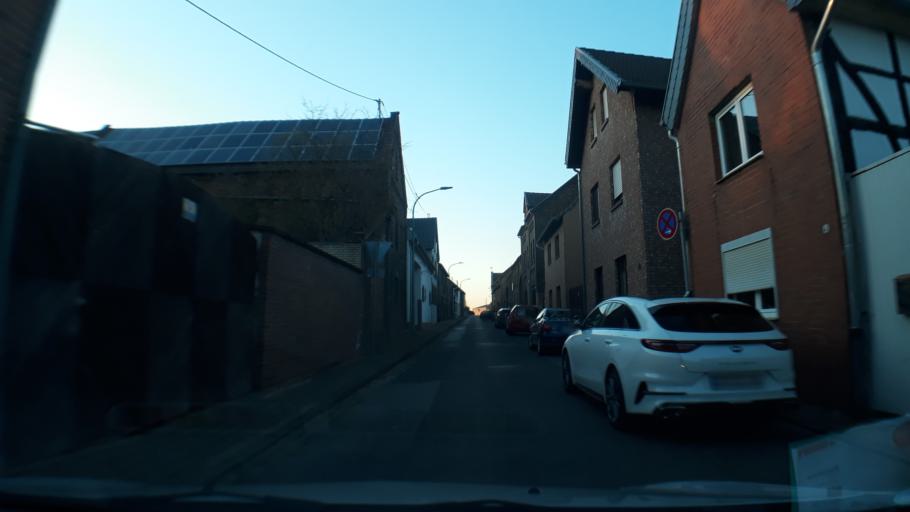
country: DE
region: North Rhine-Westphalia
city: Zulpich
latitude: 50.7028
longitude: 6.6207
